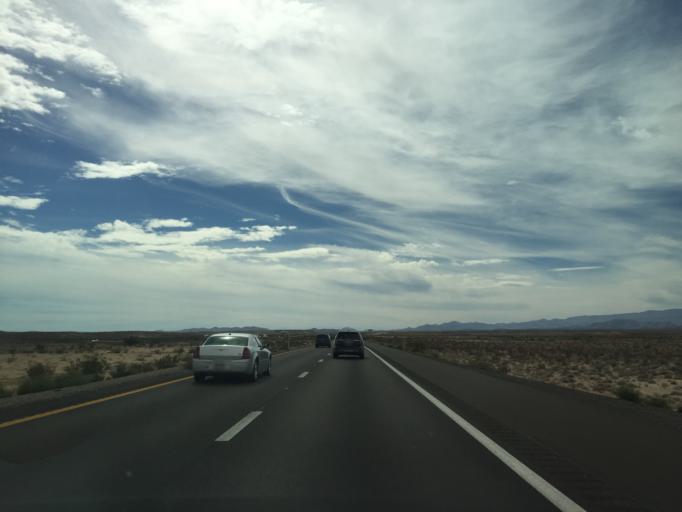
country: US
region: Nevada
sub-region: Clark County
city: Moapa Town
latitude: 36.5655
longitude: -114.6788
